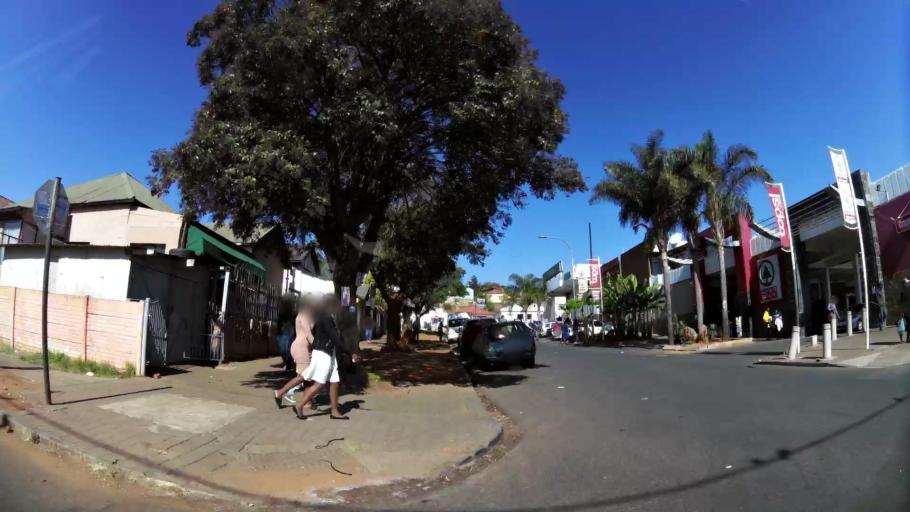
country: ZA
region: Gauteng
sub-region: City of Johannesburg Metropolitan Municipality
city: Johannesburg
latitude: -26.1965
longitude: 28.0686
